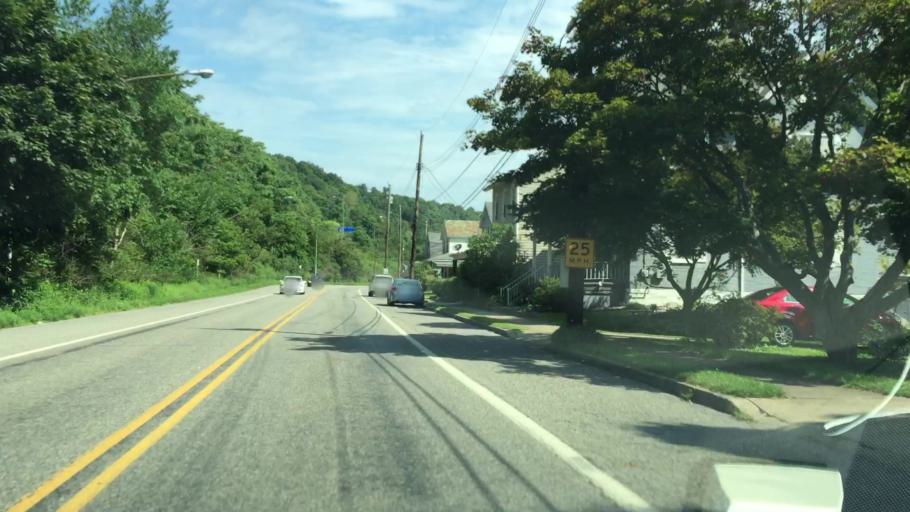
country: US
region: Pennsylvania
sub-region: Allegheny County
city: Coraopolis
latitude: 40.5234
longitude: -80.1303
